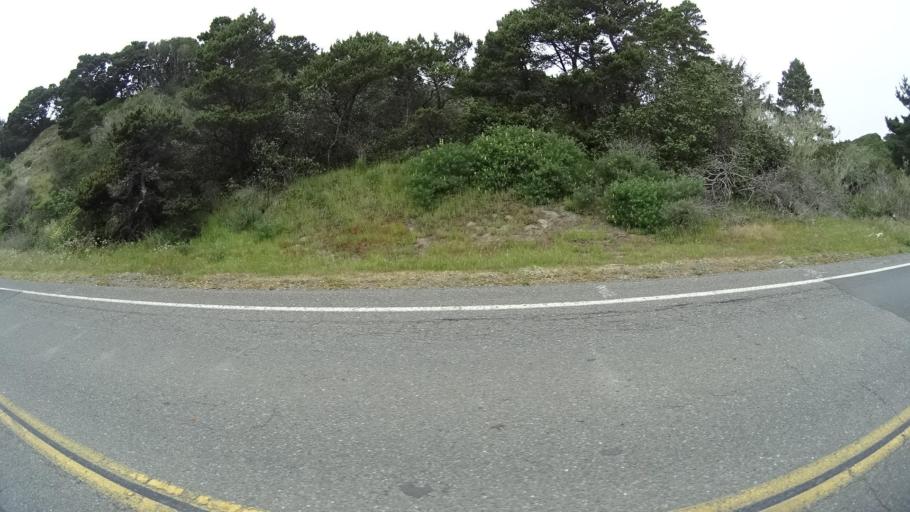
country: US
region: California
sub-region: Humboldt County
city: Eureka
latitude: 40.8222
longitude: -124.1869
